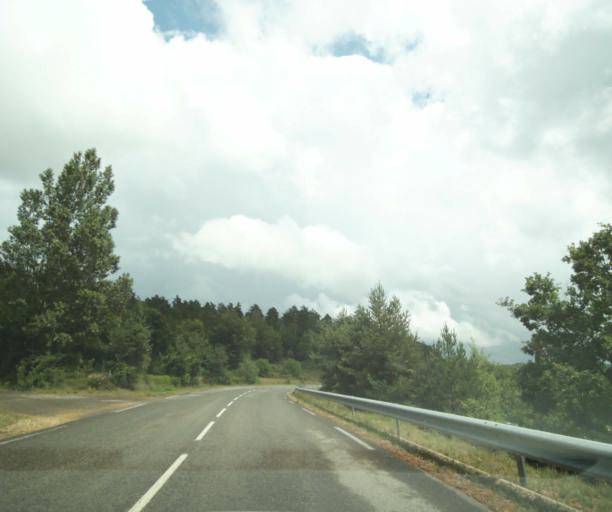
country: FR
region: Languedoc-Roussillon
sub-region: Departement de la Lozere
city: La Canourgue
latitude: 44.4094
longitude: 3.1653
